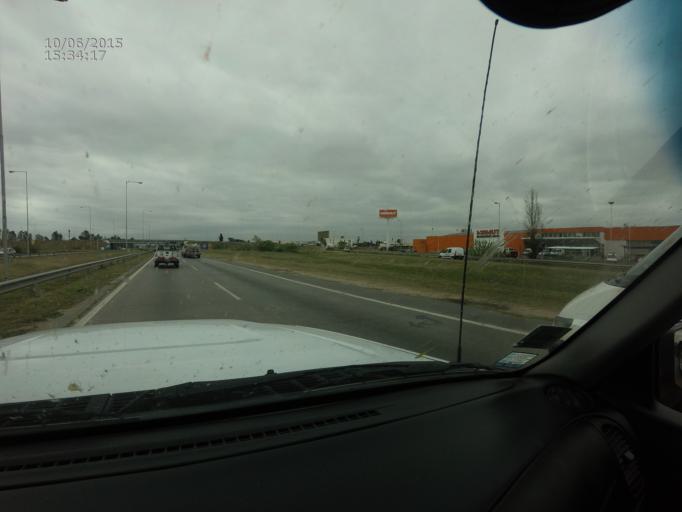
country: AR
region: Cordoba
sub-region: Departamento de Capital
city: Cordoba
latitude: -31.3580
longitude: -64.1734
